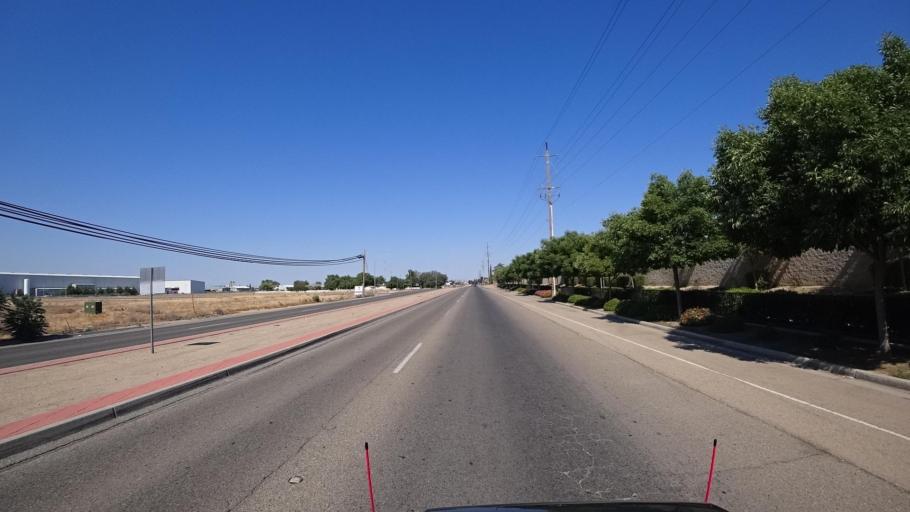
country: US
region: California
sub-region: Fresno County
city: Sunnyside
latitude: 36.7073
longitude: -119.7297
